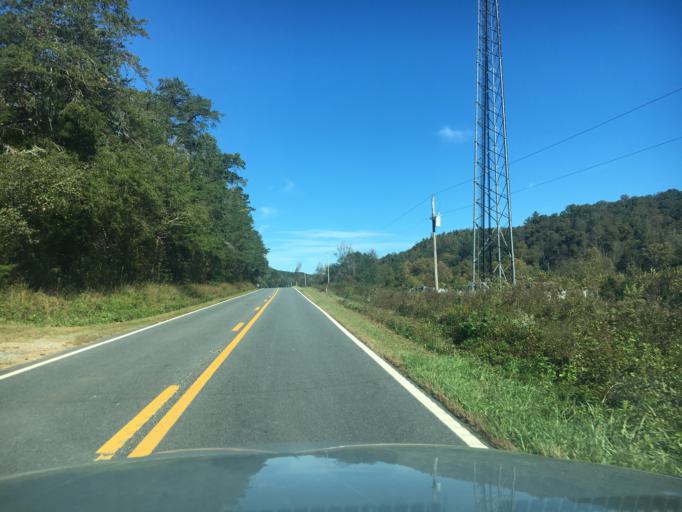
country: US
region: North Carolina
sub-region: Rutherford County
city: Spindale
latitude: 35.5352
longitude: -81.8563
